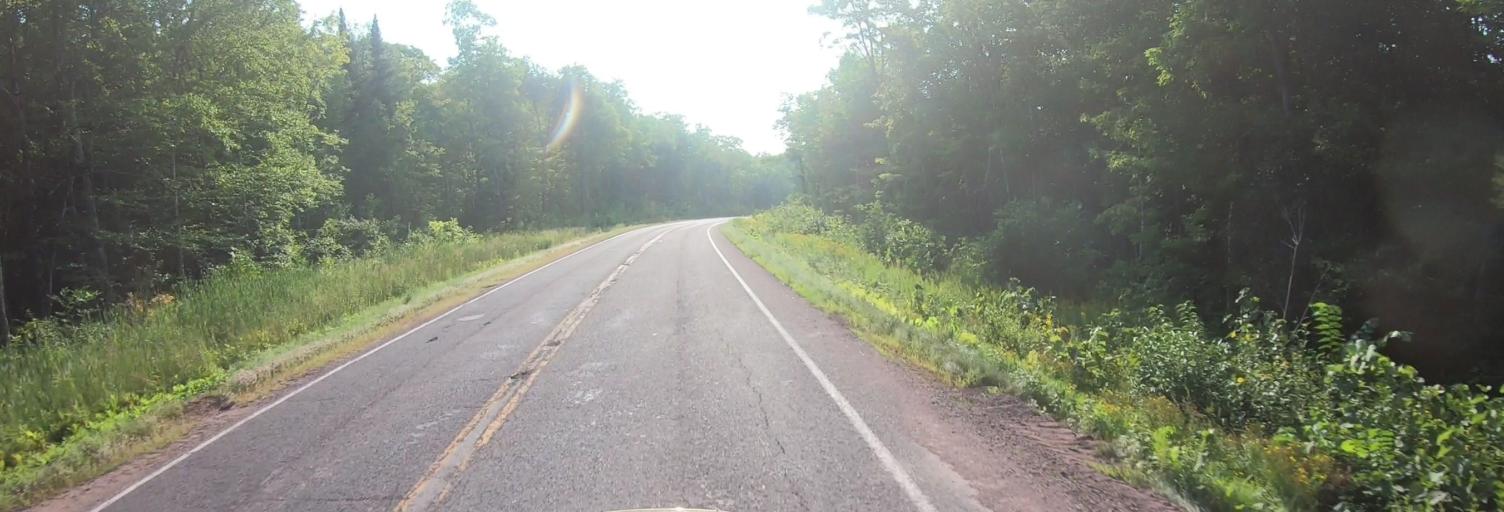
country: US
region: Wisconsin
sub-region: Ashland County
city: Ashland
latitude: 46.3029
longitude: -90.7666
